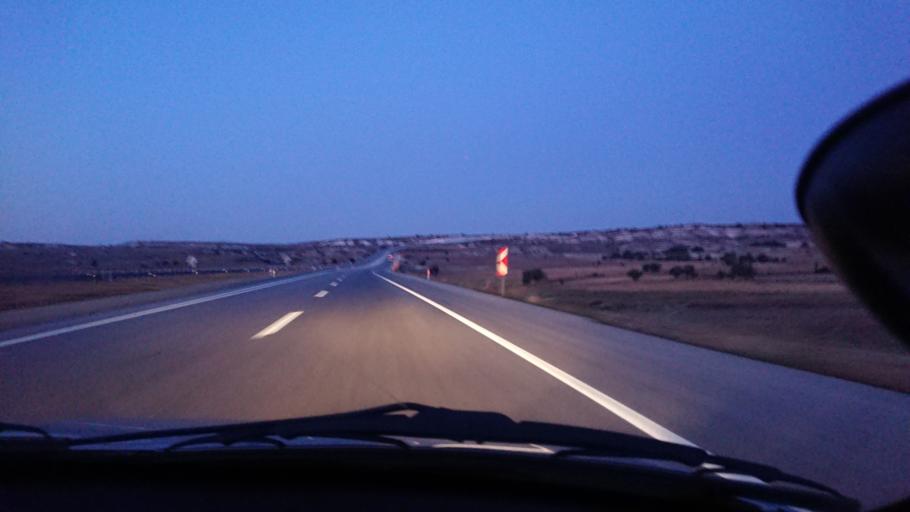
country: TR
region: Kuetahya
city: Cavdarhisar
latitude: 39.1327
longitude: 29.5524
